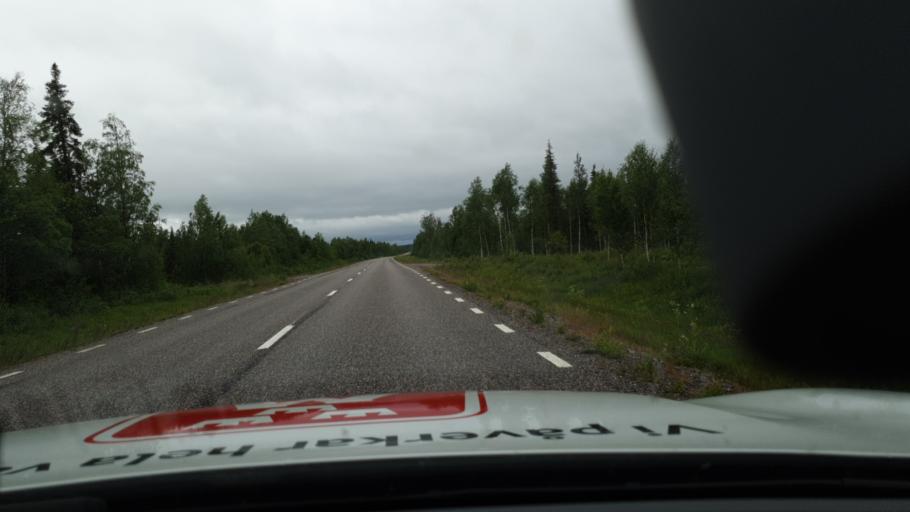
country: SE
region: Norrbotten
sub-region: Pajala Kommun
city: Pajala
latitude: 67.1244
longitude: 23.5984
